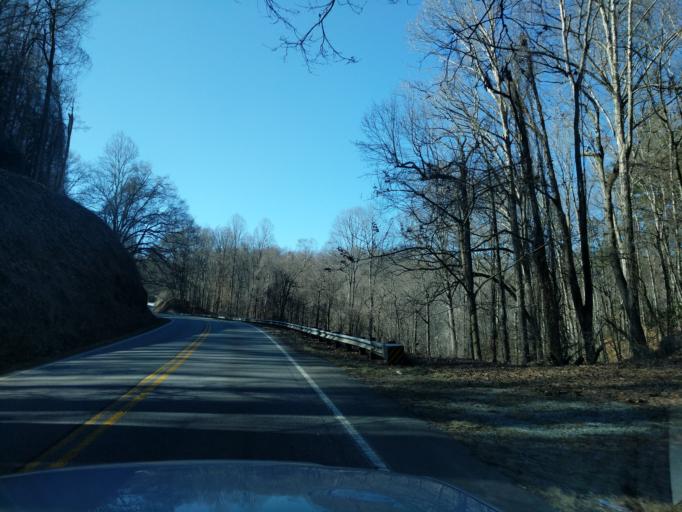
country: US
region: North Carolina
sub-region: Swain County
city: Bryson City
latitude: 35.3375
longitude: -83.5689
